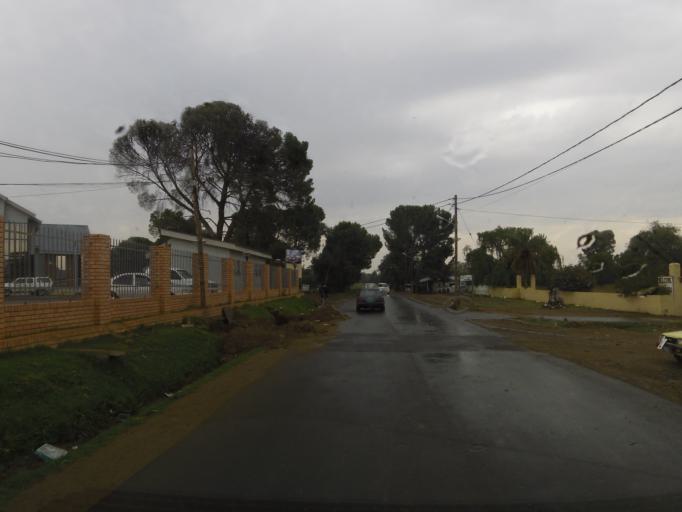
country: LS
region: Mafeteng
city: Mafeteng
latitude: -29.8209
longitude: 27.2405
